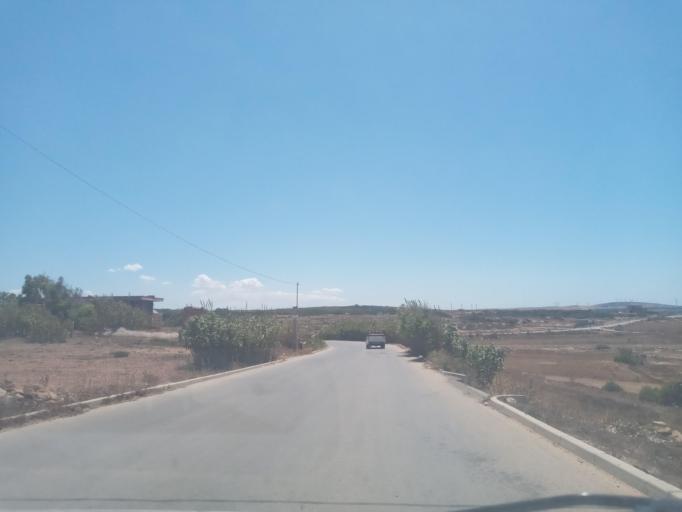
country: TN
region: Nabul
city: El Haouaria
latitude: 37.0528
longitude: 10.9900
